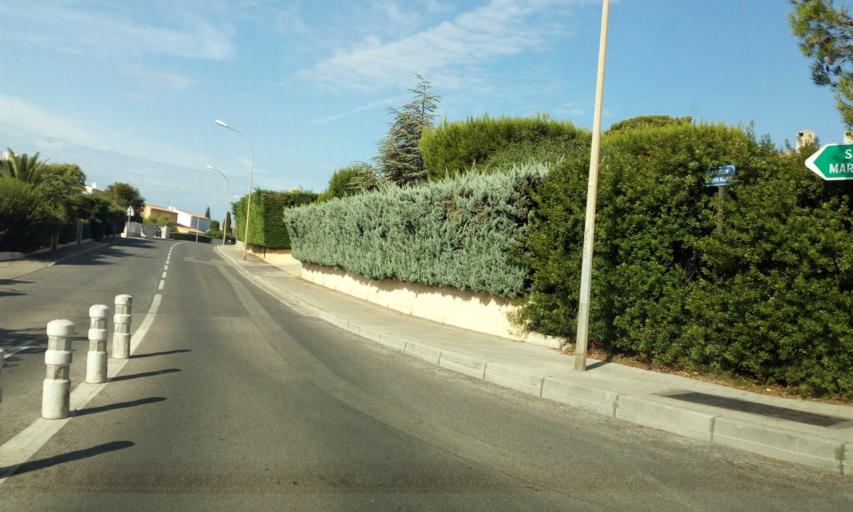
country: FR
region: Provence-Alpes-Cote d'Azur
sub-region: Departement du Var
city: Bandol
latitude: 43.1433
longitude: 5.7537
